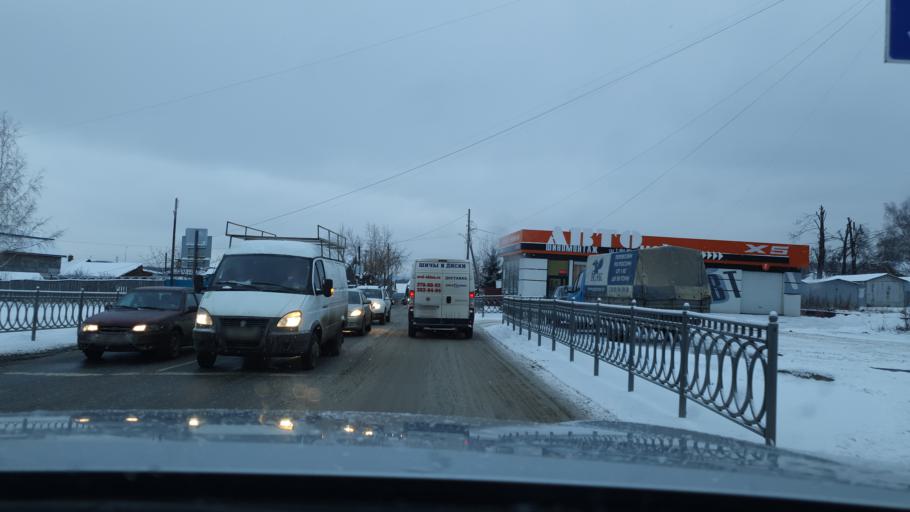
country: RU
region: Sverdlovsk
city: Istok
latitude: 56.7838
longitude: 60.7433
